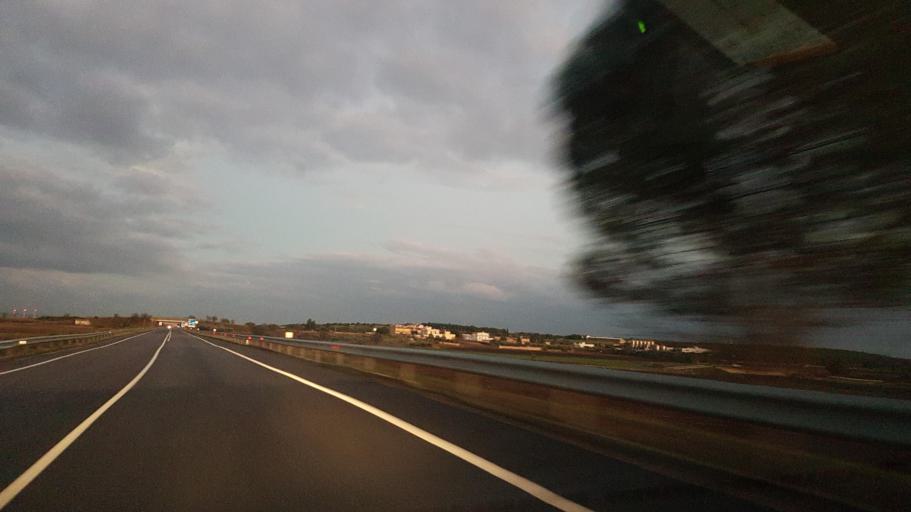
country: IT
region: Apulia
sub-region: Provincia di Taranto
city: Laterza
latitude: 40.6498
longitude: 16.8119
